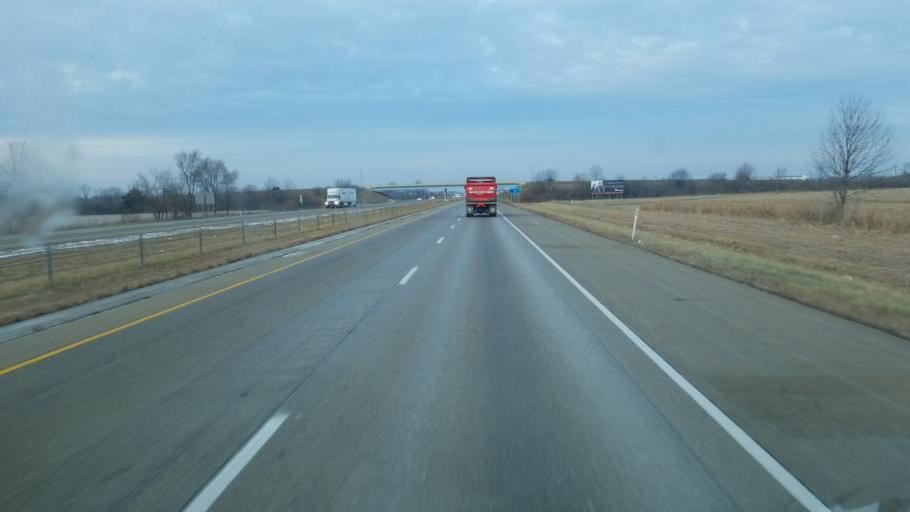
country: US
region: Indiana
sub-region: Marion County
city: Cumberland
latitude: 39.8199
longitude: -85.8748
